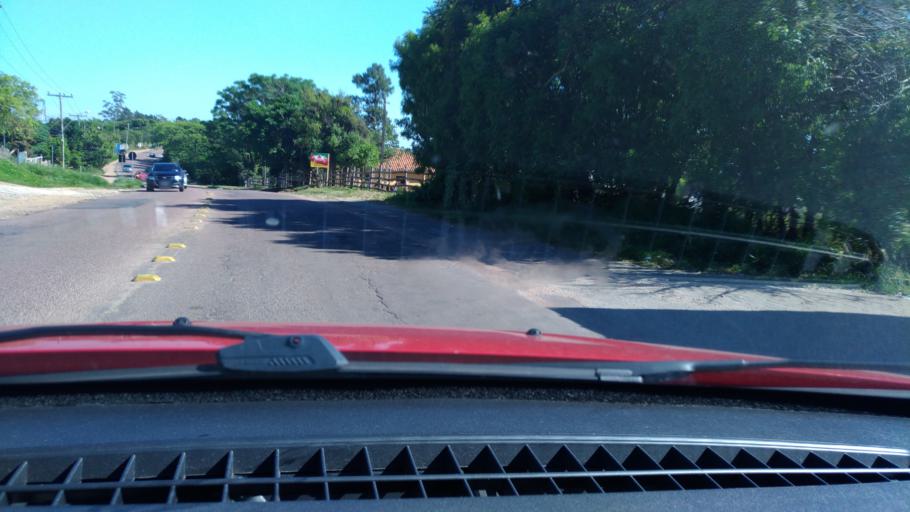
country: BR
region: Rio Grande do Sul
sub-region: Viamao
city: Viamao
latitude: -30.0614
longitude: -51.0566
